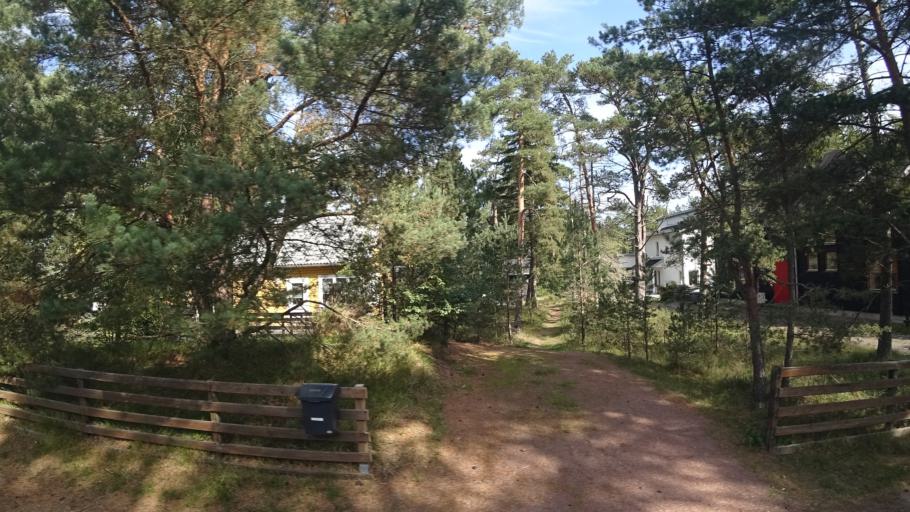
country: SE
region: Skane
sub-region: Kristianstads Kommun
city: Ahus
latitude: 55.9166
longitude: 14.2972
